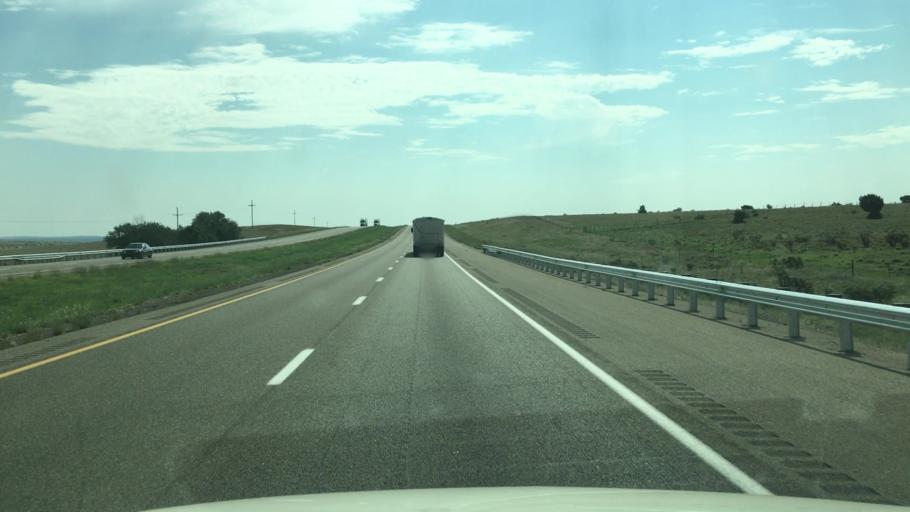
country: US
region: New Mexico
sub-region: Guadalupe County
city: Santa Rosa
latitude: 34.9820
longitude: -105.1049
